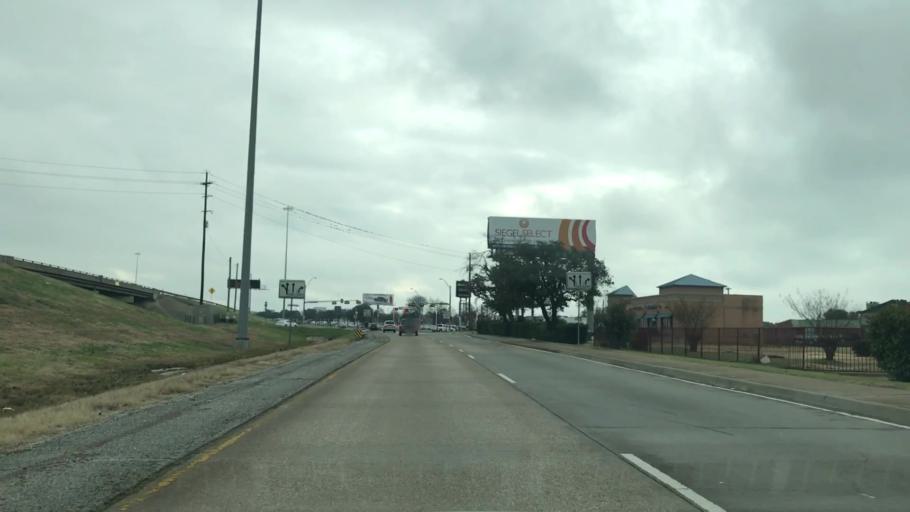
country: US
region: Texas
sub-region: Dallas County
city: Garland
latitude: 32.8751
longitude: -96.6845
